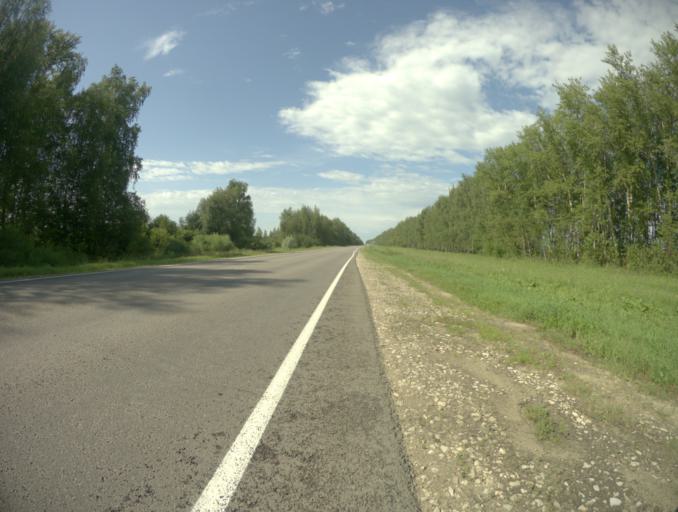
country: RU
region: Vladimir
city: Suzdal'
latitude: 56.3890
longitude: 40.4528
